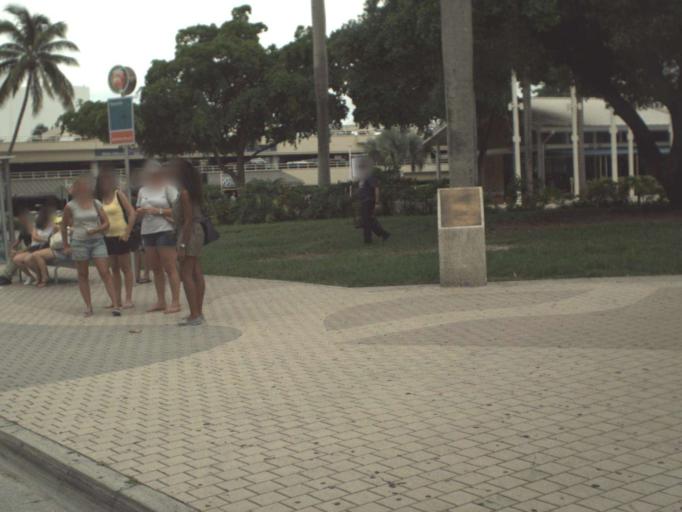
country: US
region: Florida
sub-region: Miami-Dade County
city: Miami
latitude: 25.7778
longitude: -80.1879
